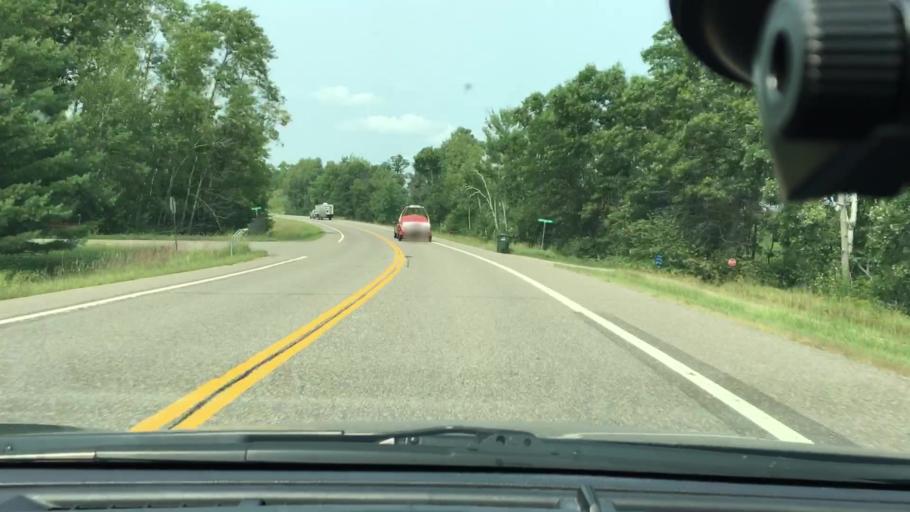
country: US
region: Minnesota
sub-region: Cass County
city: East Gull Lake
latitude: 46.4015
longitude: -94.3507
